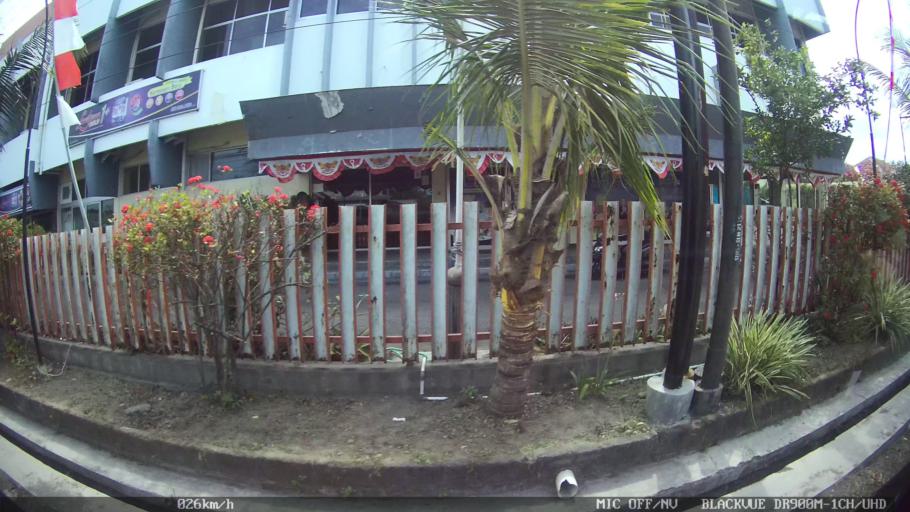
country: ID
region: Daerah Istimewa Yogyakarta
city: Depok
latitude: -7.7797
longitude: 110.4347
